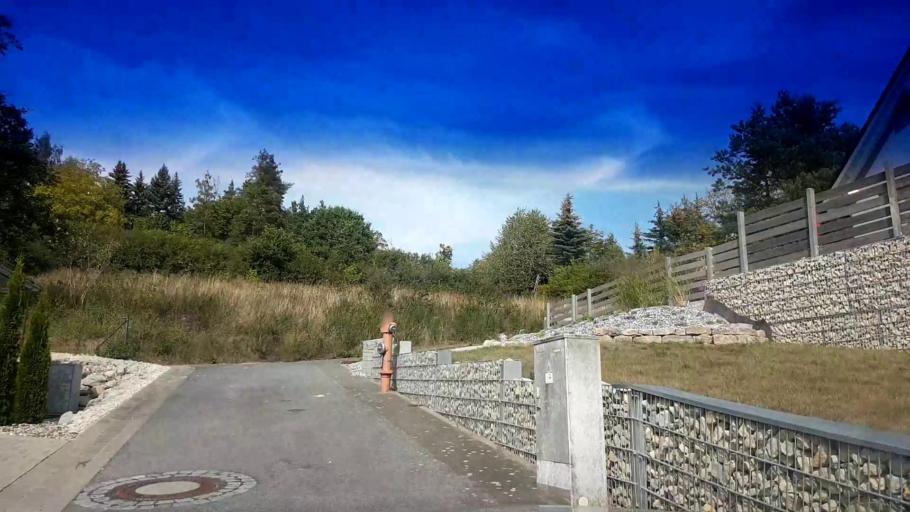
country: DE
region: Bavaria
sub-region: Upper Franconia
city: Oberhaid
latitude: 49.9387
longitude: 10.8045
